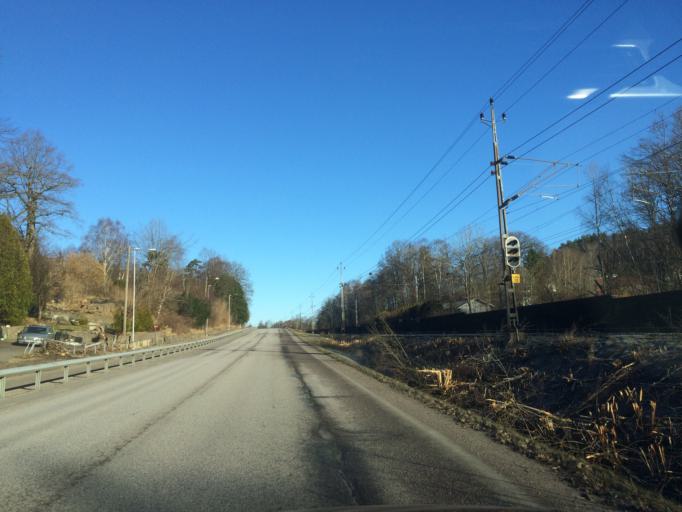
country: SE
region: Vaestra Goetaland
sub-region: Molndal
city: Lindome
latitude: 57.5805
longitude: 12.0759
